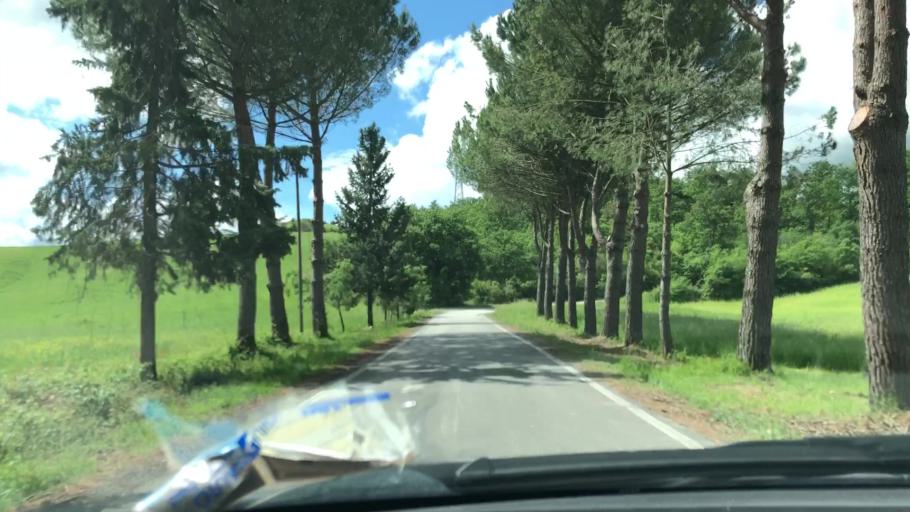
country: IT
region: Tuscany
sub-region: Province of Pisa
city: Saline
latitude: 43.3479
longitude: 10.7923
